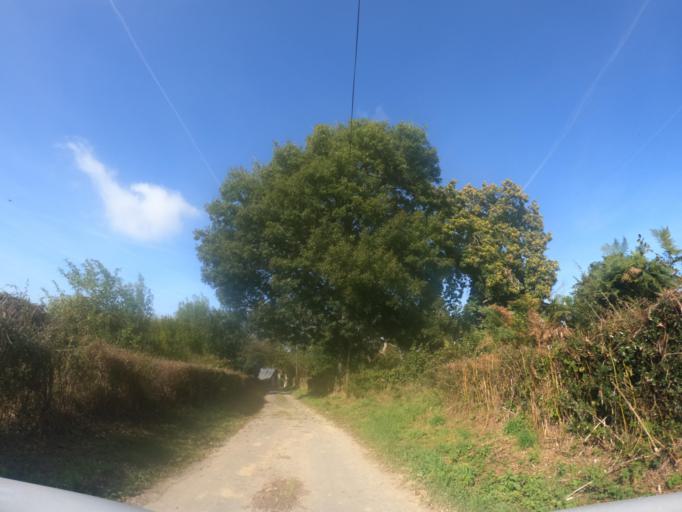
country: FR
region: Poitou-Charentes
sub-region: Departement des Deux-Sevres
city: Courlay
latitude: 46.7891
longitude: -0.5687
